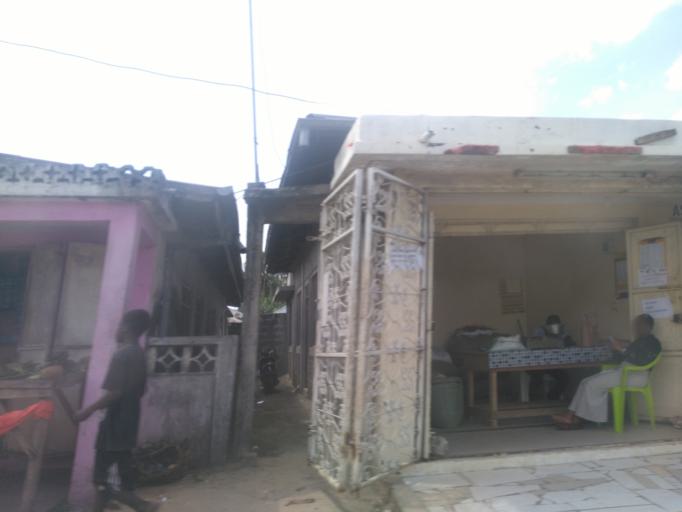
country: TZ
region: Zanzibar Urban/West
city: Zanzibar
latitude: -6.1731
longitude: 39.2086
